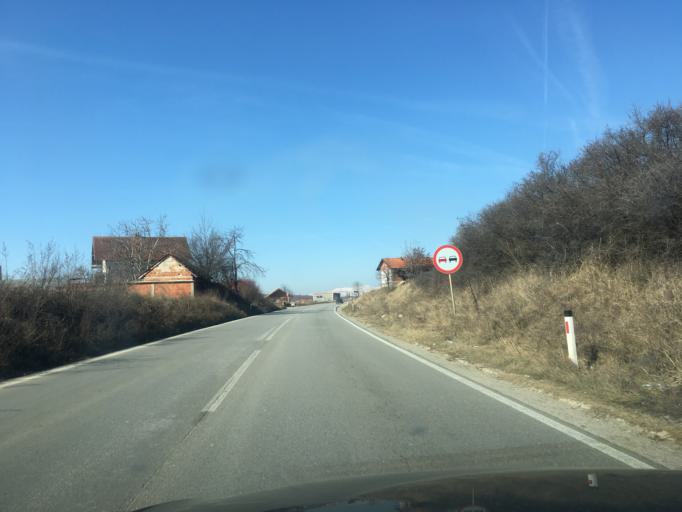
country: XK
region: Prizren
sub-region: Komuna e Malisheves
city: Llazice
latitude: 42.5781
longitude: 20.7007
